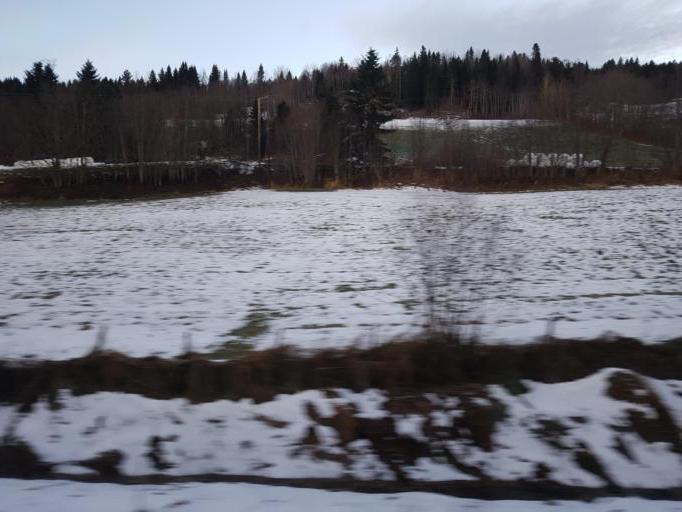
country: NO
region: Sor-Trondelag
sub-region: Midtre Gauldal
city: Storen
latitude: 62.9498
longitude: 10.1874
